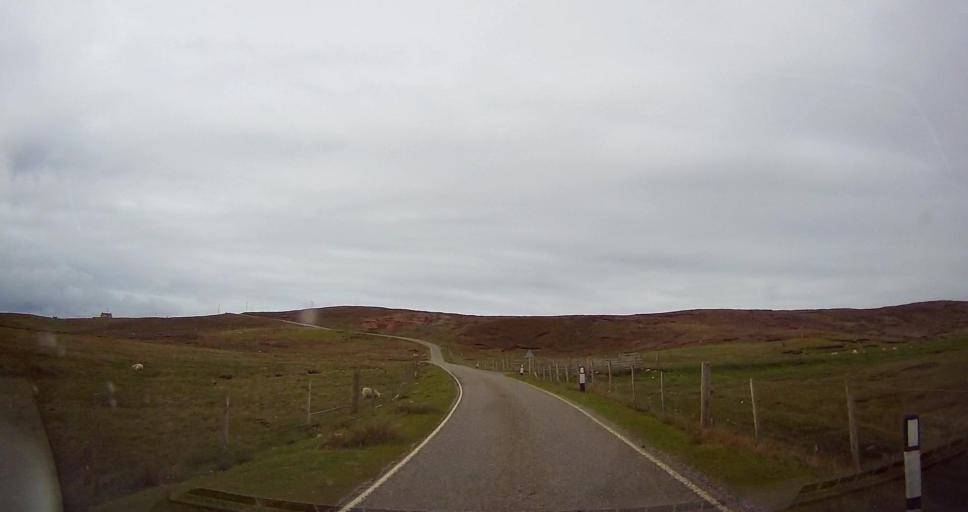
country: GB
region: Scotland
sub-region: Shetland Islands
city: Lerwick
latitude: 60.4867
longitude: -1.5102
